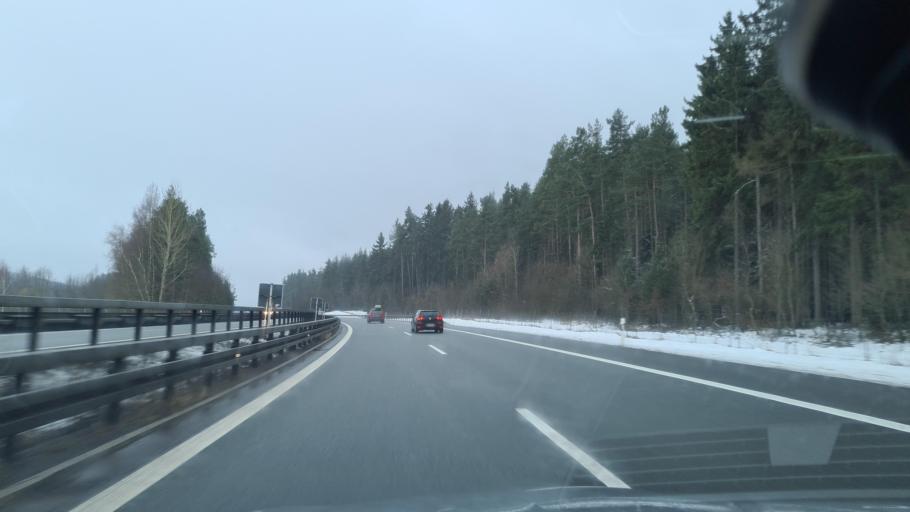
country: DE
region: Bavaria
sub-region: Upper Franconia
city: Thiersheim
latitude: 50.0638
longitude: 12.0974
